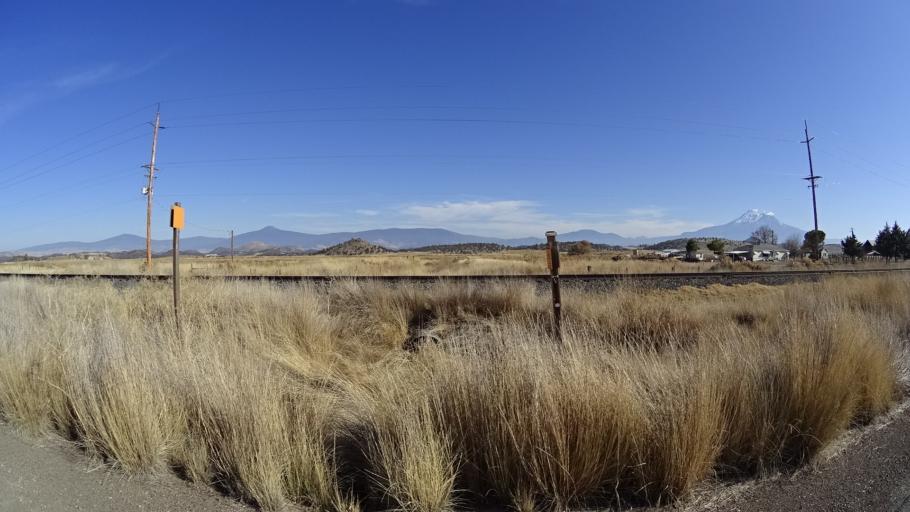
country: US
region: California
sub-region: Siskiyou County
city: Montague
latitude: 41.6334
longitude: -122.5220
